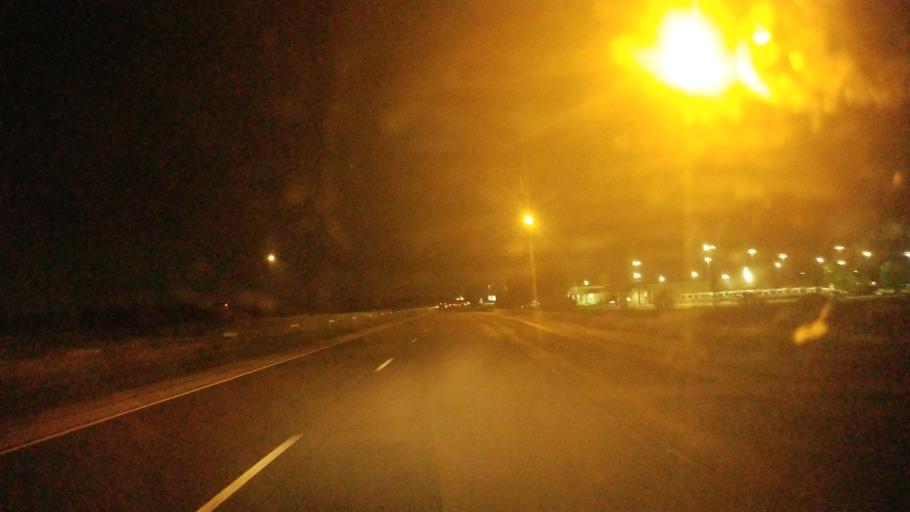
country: US
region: Illinois
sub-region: Madison County
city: Mitchell
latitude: 38.7578
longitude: -90.0718
